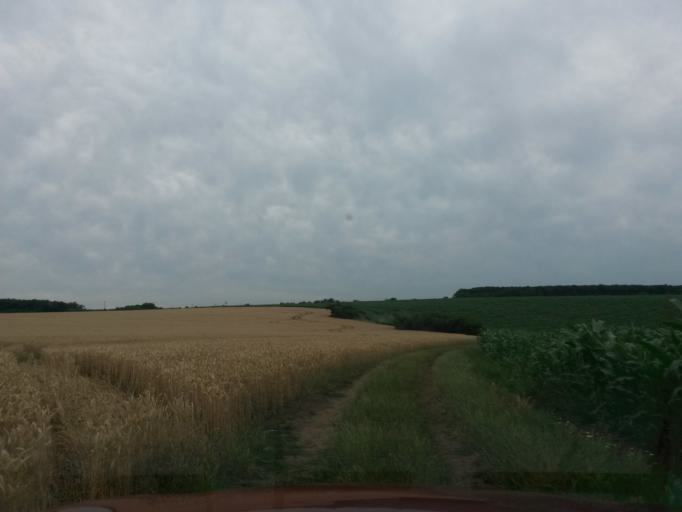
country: SK
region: Nitriansky
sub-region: Okres Nitra
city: Nitra
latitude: 48.3472
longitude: 17.9852
